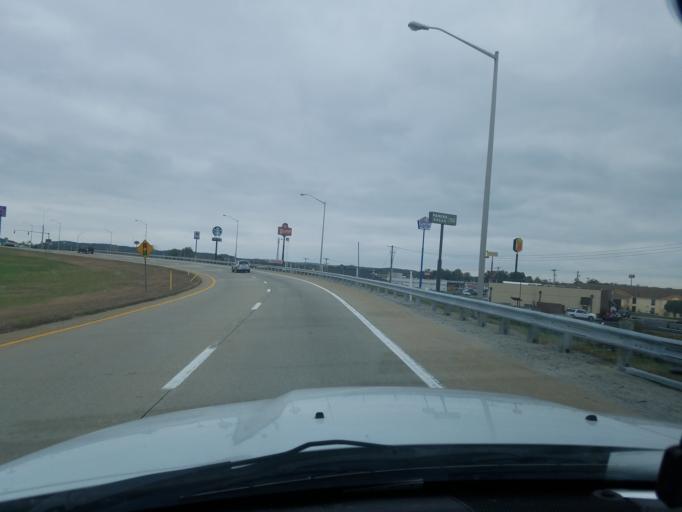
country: US
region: Kentucky
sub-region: Bullitt County
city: Shepherdsville
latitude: 37.9940
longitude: -85.7064
